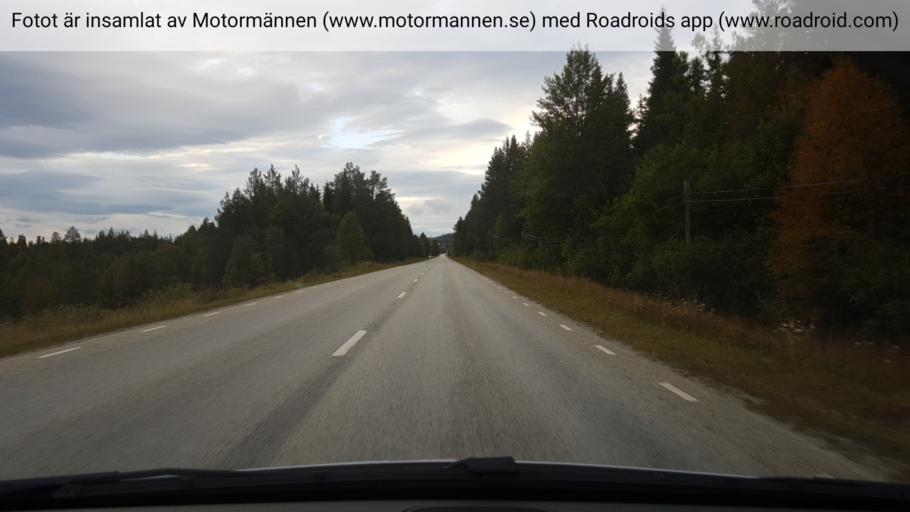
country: SE
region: Jaemtland
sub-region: Bergs Kommun
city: Hoverberg
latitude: 62.5106
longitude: 14.1955
